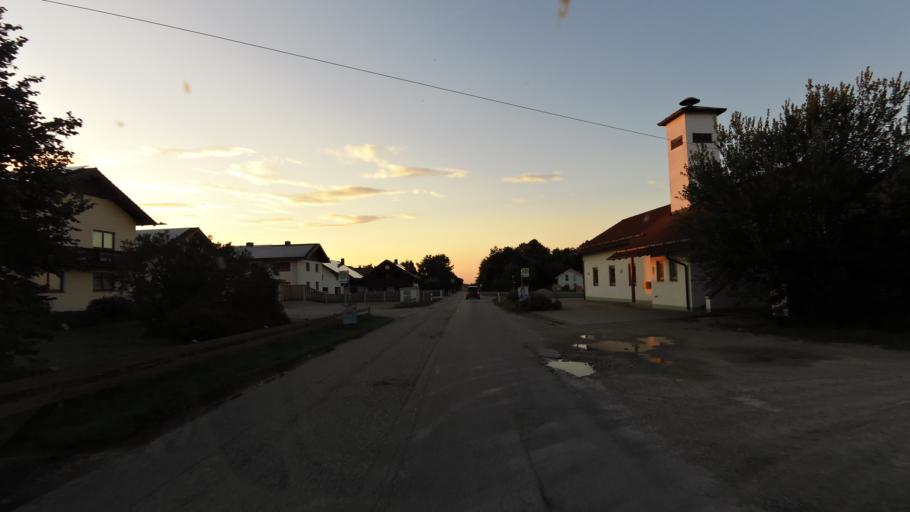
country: DE
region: Bavaria
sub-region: Upper Bavaria
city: Taufkirchen
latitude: 48.1285
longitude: 12.4618
